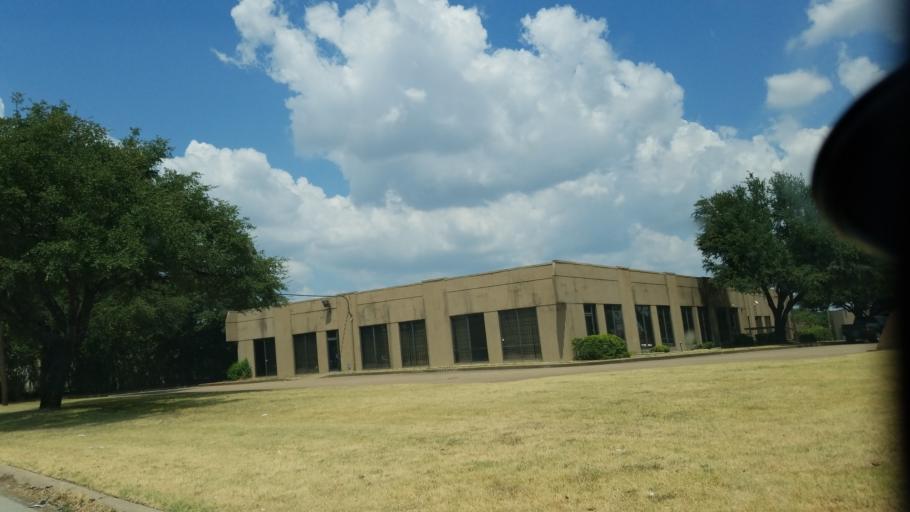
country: US
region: Texas
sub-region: Dallas County
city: Duncanville
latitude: 32.6873
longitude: -96.8828
